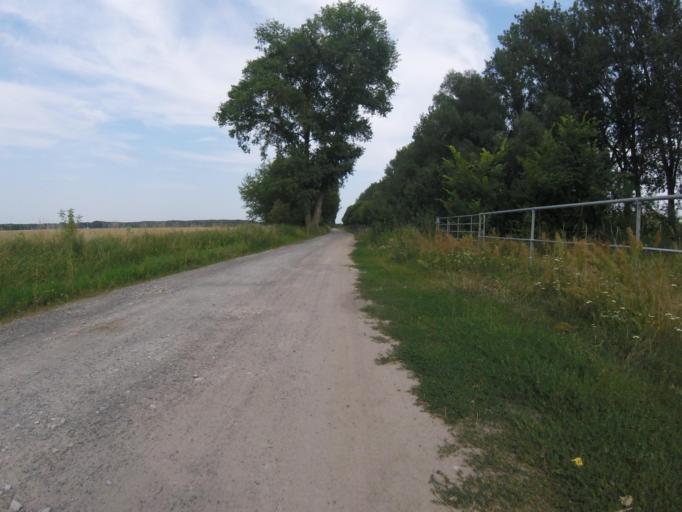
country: DE
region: Brandenburg
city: Erkner
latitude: 52.3066
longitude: 13.7670
